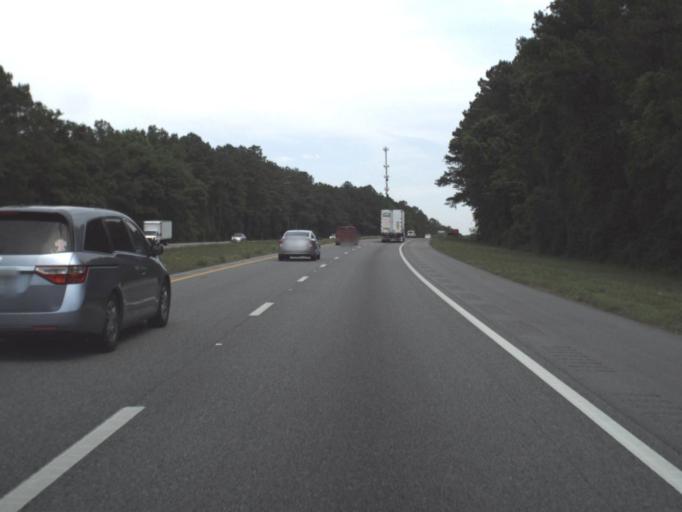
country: US
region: Florida
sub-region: Suwannee County
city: Live Oak
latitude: 30.3485
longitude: -82.9936
